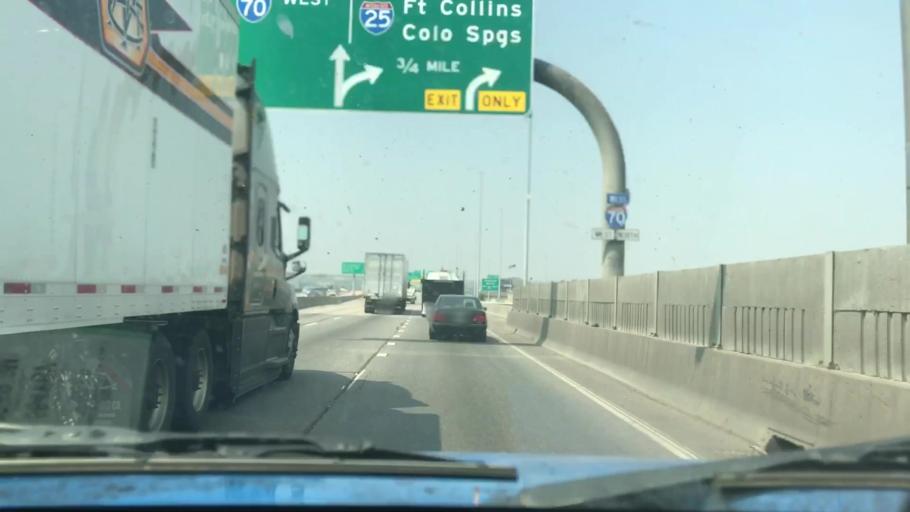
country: US
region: Colorado
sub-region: Adams County
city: Commerce City
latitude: 39.7802
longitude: -104.9663
